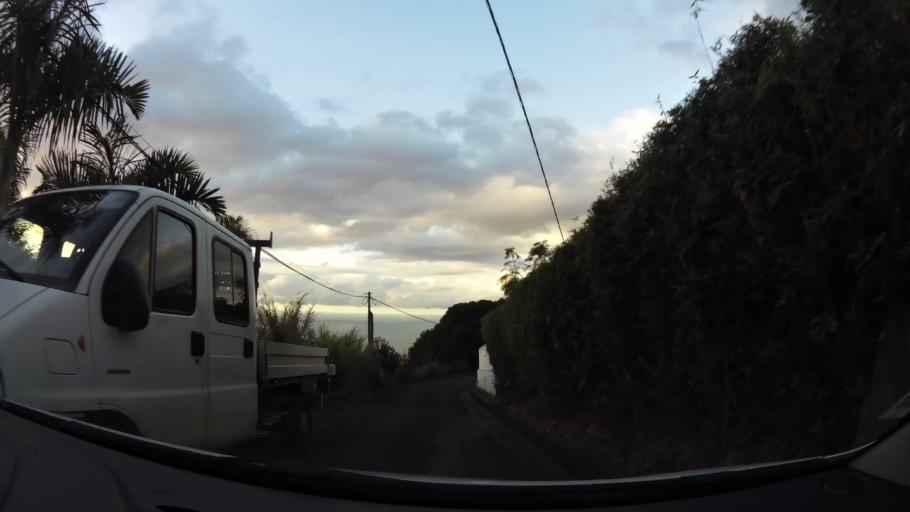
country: RE
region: Reunion
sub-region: Reunion
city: Saint-Denis
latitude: -20.9209
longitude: 55.4639
